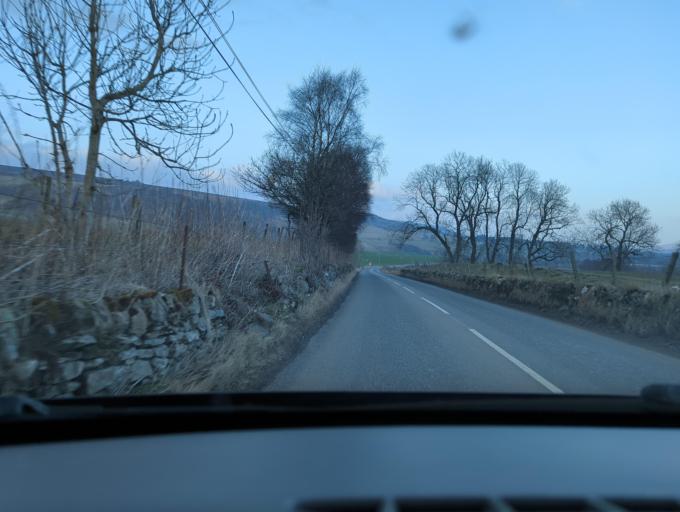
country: GB
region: Scotland
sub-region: Perth and Kinross
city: Methven
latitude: 56.5319
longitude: -3.7111
